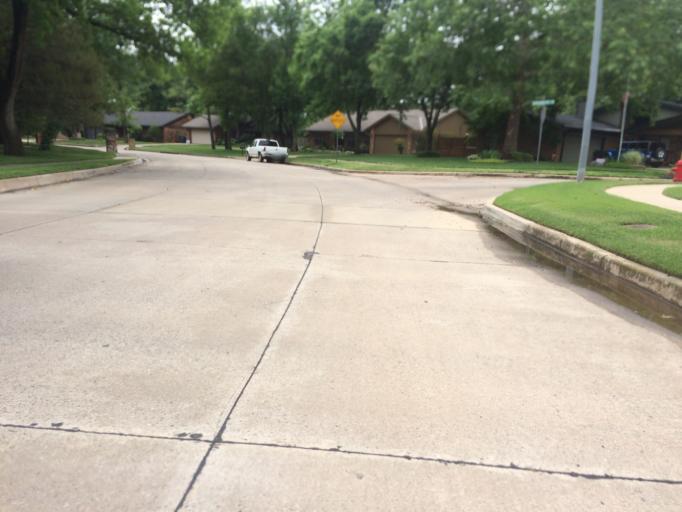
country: US
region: Oklahoma
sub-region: Cleveland County
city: Norman
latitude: 35.1842
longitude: -97.4559
